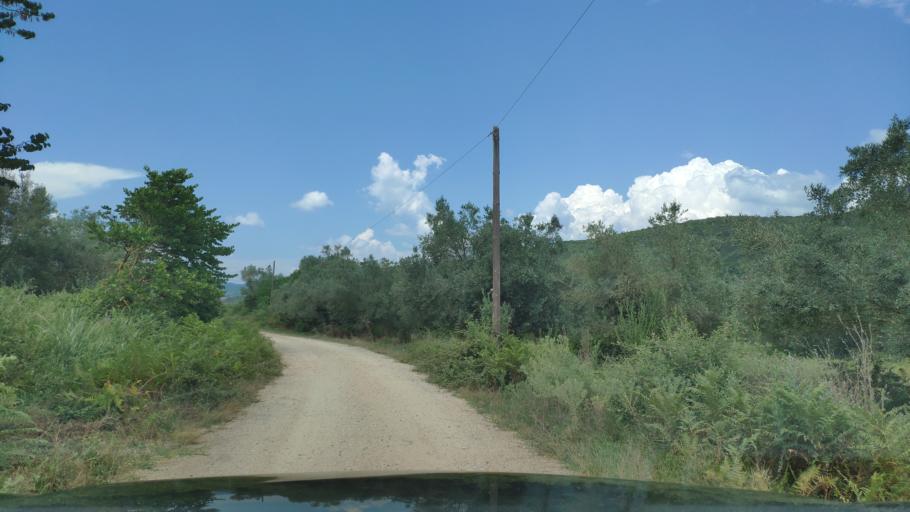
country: GR
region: West Greece
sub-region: Nomos Aitolias kai Akarnanias
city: Menidi
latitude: 39.0602
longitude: 21.0944
